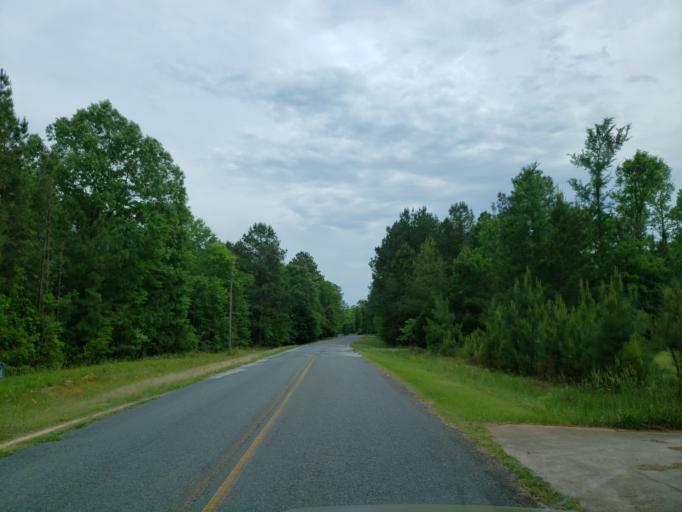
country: US
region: Georgia
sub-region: Bibb County
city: West Point
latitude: 32.8520
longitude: -83.8911
